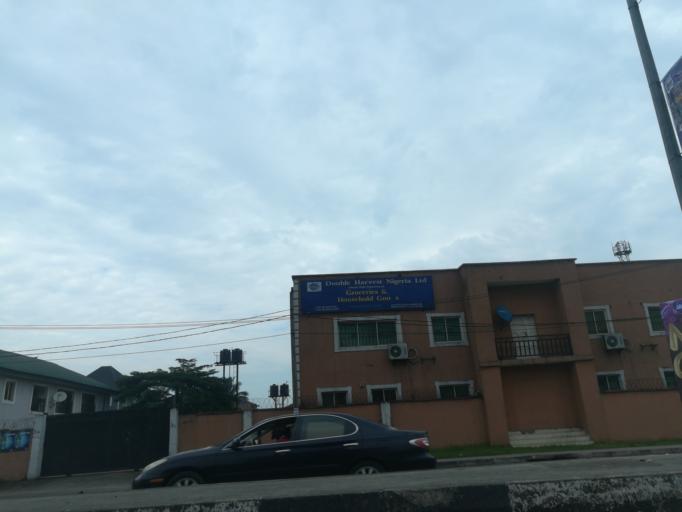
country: NG
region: Rivers
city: Port Harcourt
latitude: 4.8348
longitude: 6.9769
